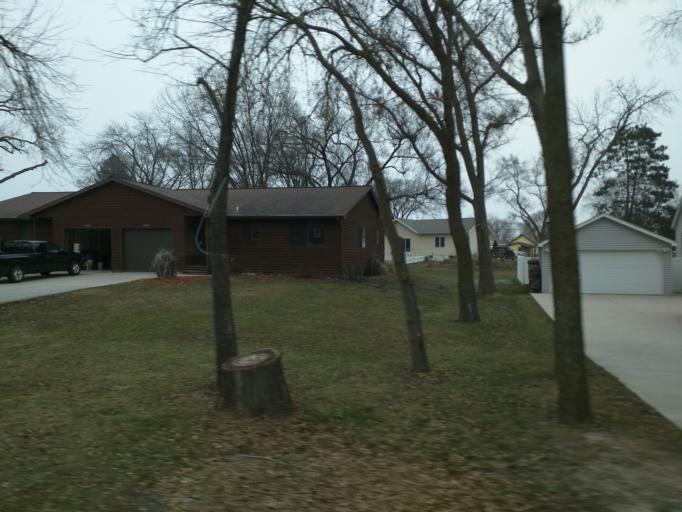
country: US
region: Wisconsin
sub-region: La Crosse County
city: French Island
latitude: 43.8462
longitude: -91.2650
